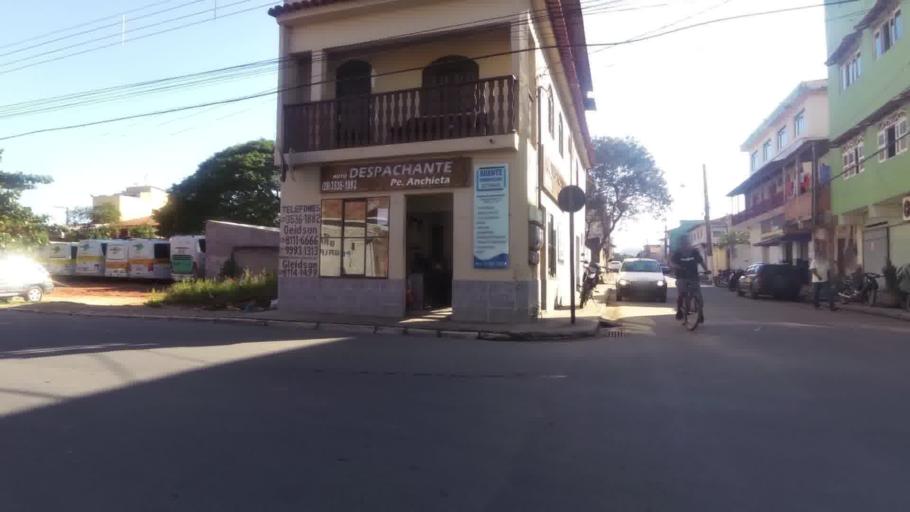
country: BR
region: Espirito Santo
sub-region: Piuma
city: Piuma
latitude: -20.8073
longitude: -40.6466
